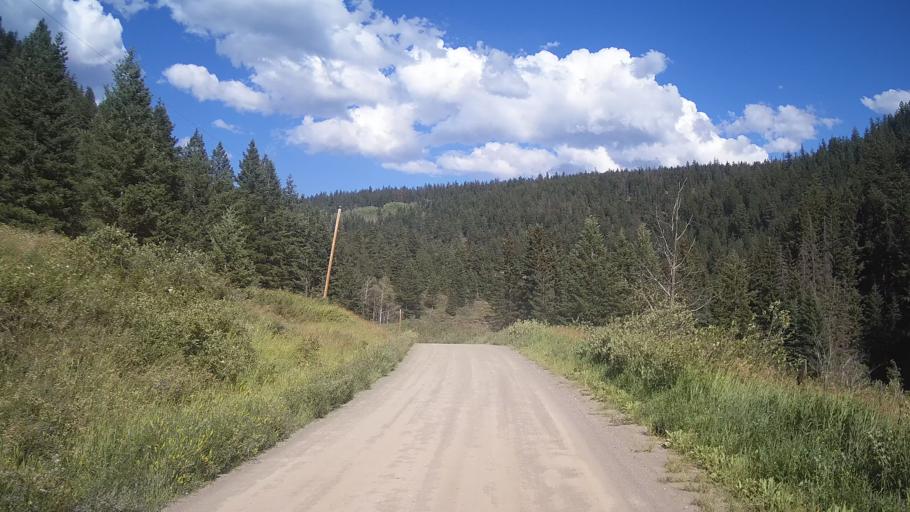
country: CA
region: British Columbia
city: Lillooet
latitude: 51.2584
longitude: -121.9963
